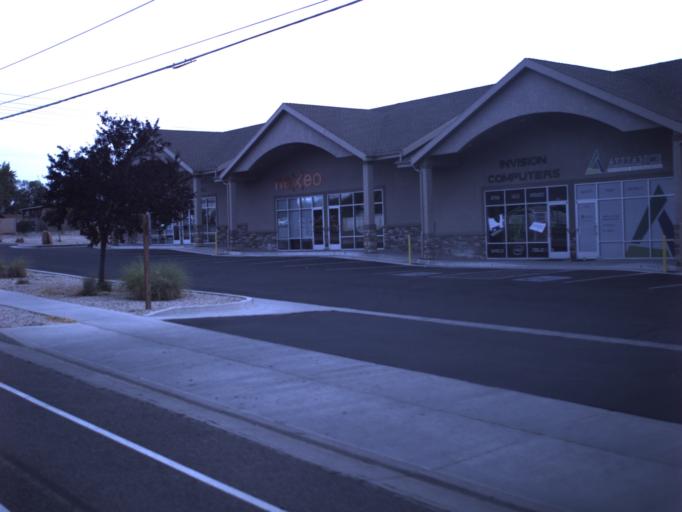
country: US
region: Utah
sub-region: Weber County
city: Roy
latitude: 41.1794
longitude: -112.0261
